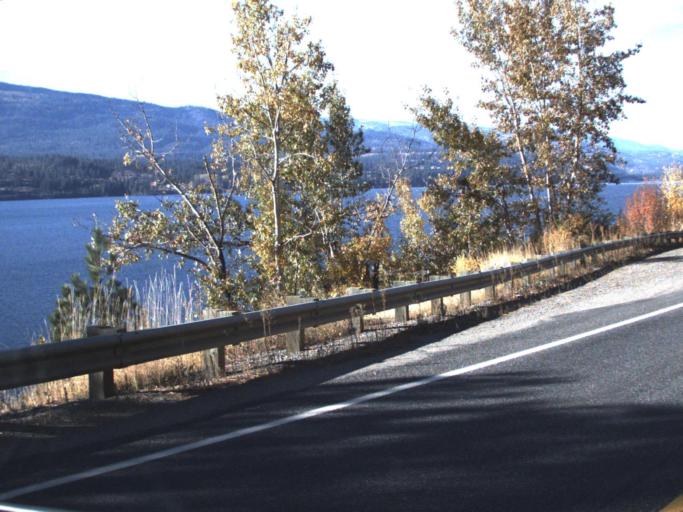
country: US
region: Washington
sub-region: Stevens County
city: Kettle Falls
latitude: 48.6365
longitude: -118.0811
